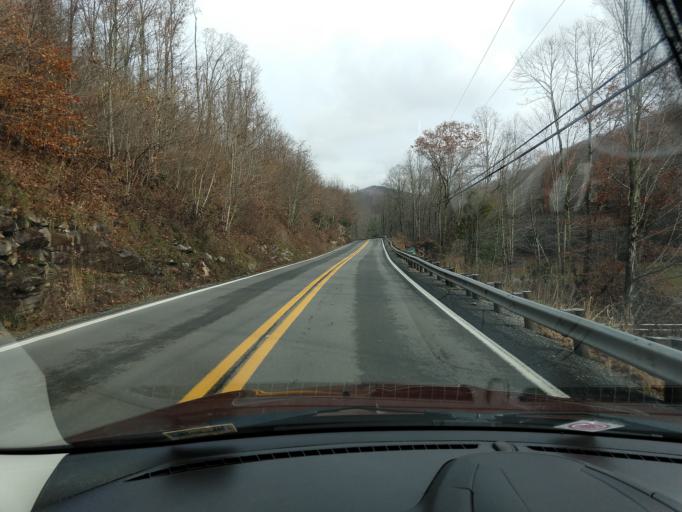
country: US
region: West Virginia
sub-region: Greenbrier County
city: Rainelle
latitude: 38.0884
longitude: -80.7069
